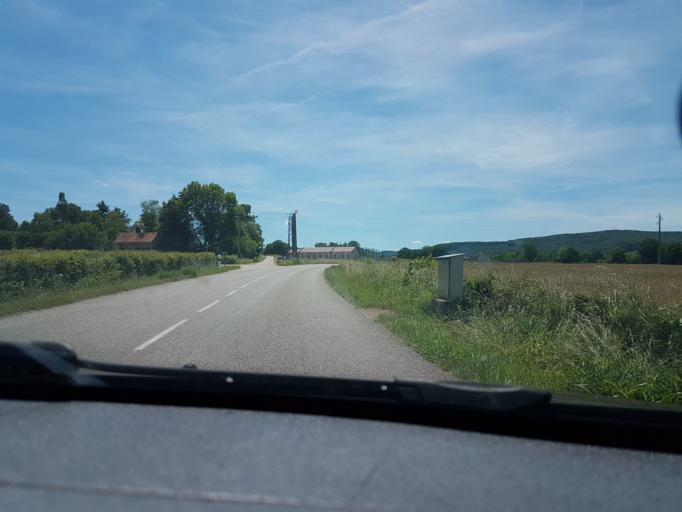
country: FR
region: Bourgogne
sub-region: Departement de Saone-et-Loire
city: Epinac
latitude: 46.9793
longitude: 4.5061
